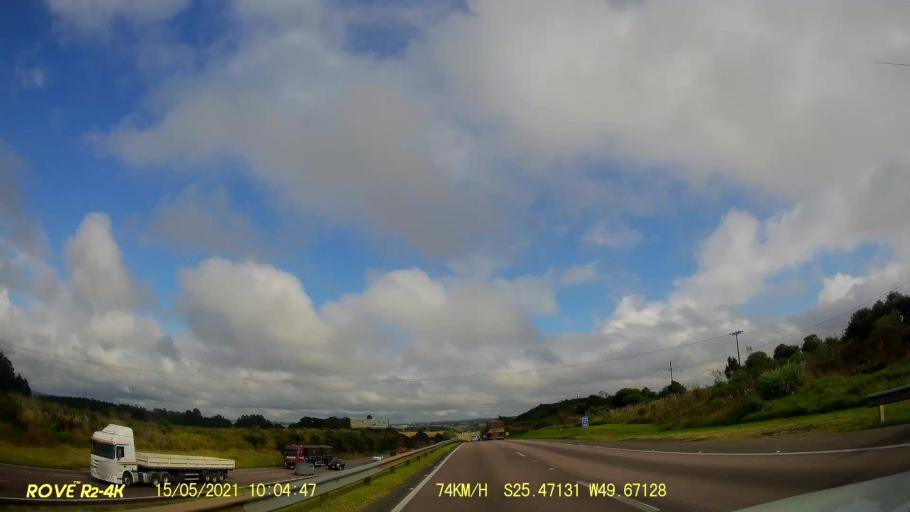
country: BR
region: Parana
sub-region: Campo Largo
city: Campo Largo
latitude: -25.4709
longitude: -49.6715
